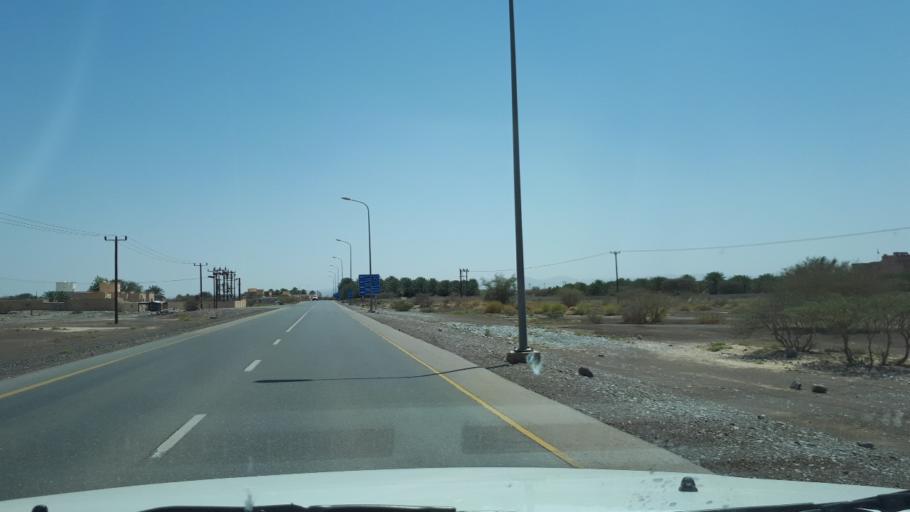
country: OM
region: Muhafazat ad Dakhiliyah
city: Bahla'
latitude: 22.9175
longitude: 57.2537
